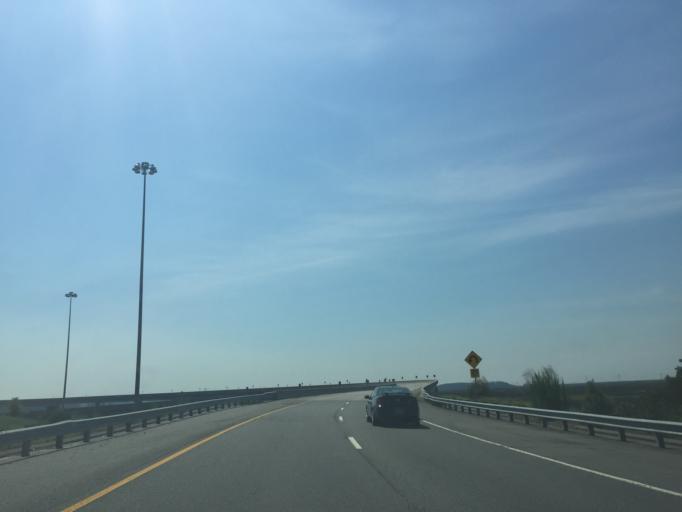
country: US
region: Georgia
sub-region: Chatham County
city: Georgetown
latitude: 31.9841
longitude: -81.2036
